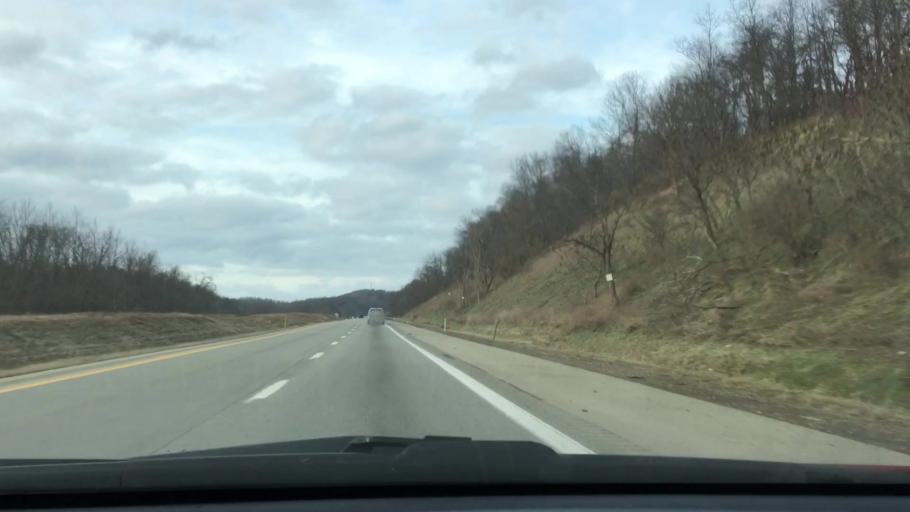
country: US
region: Pennsylvania
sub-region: Greene County
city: Waynesburg
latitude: 39.9835
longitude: -80.1815
